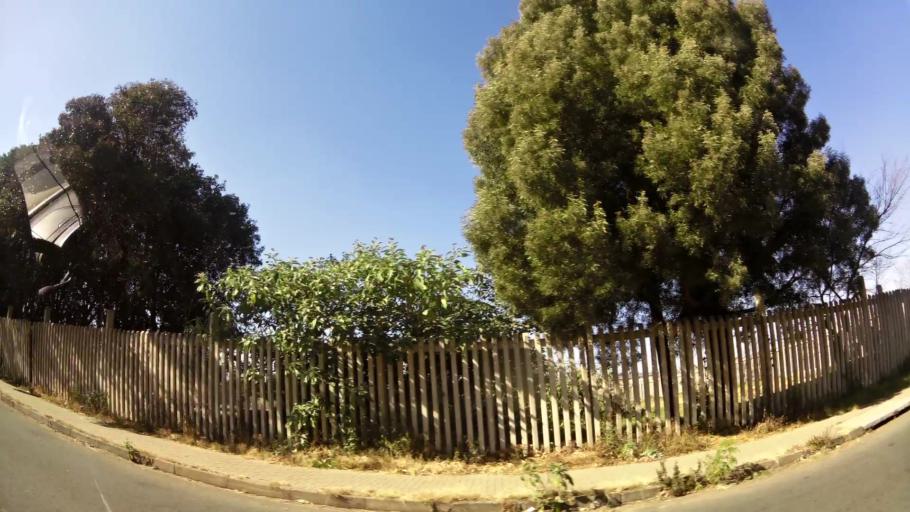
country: ZA
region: Gauteng
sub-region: City of Johannesburg Metropolitan Municipality
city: Johannesburg
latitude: -26.1783
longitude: 27.9699
